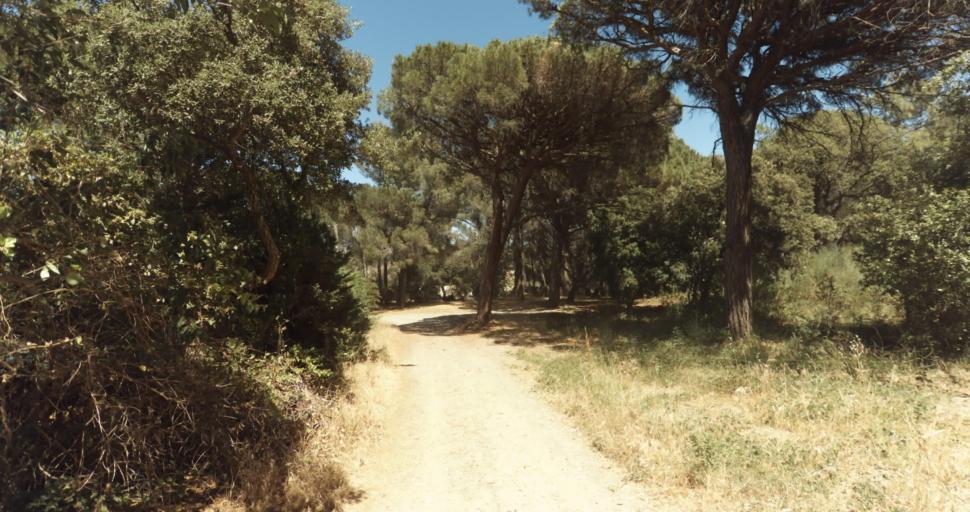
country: FR
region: Provence-Alpes-Cote d'Azur
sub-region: Departement du Var
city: Gassin
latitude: 43.2572
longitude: 6.5670
